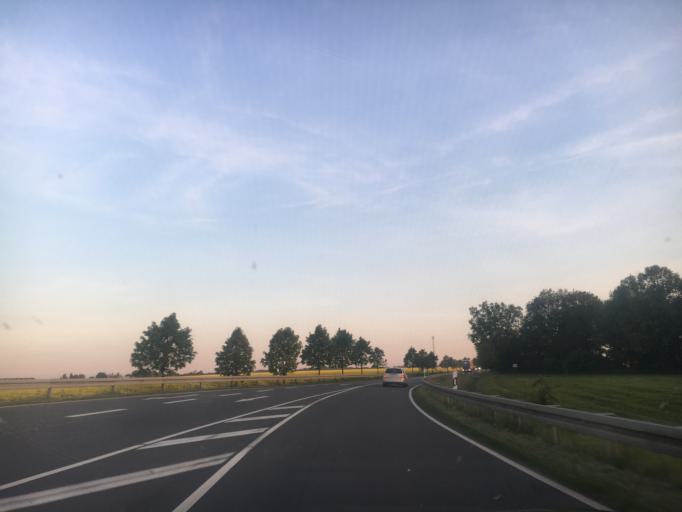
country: DE
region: Thuringia
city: Hirschfeld
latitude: 50.9898
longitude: 12.1398
